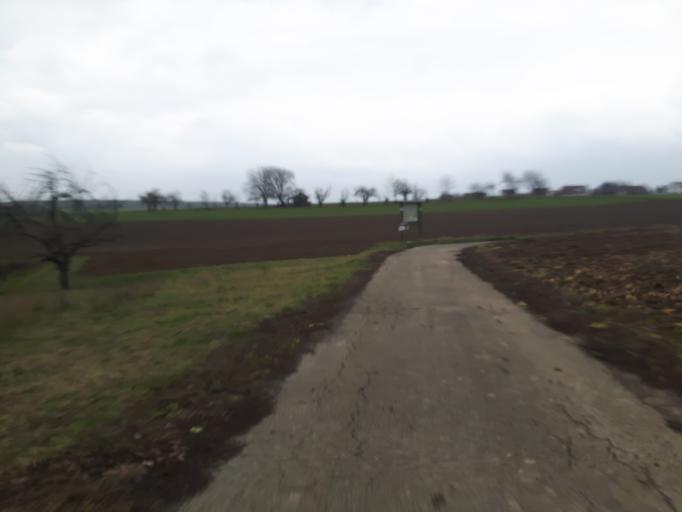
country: DE
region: Baden-Wuerttemberg
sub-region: Regierungsbezirk Stuttgart
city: Nordheim
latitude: 49.1124
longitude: 9.1483
